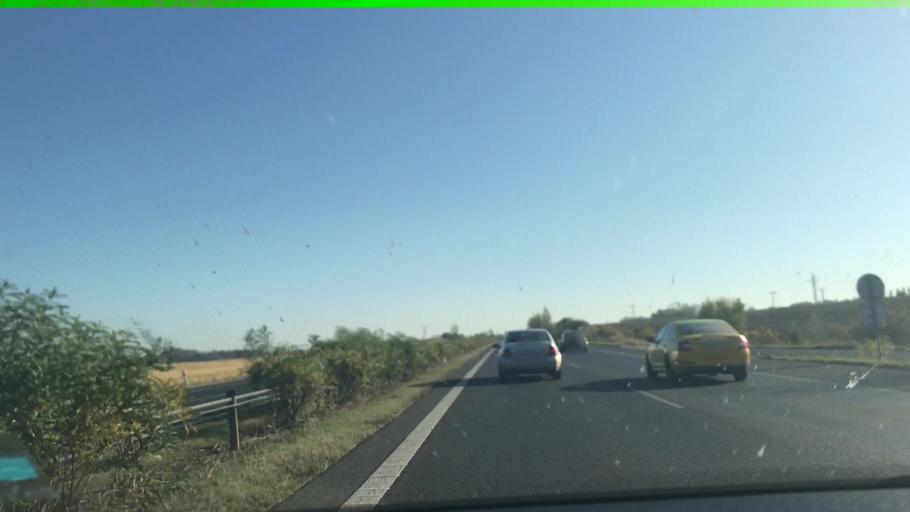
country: CZ
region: Central Bohemia
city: Velvary
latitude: 50.3472
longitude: 14.2782
